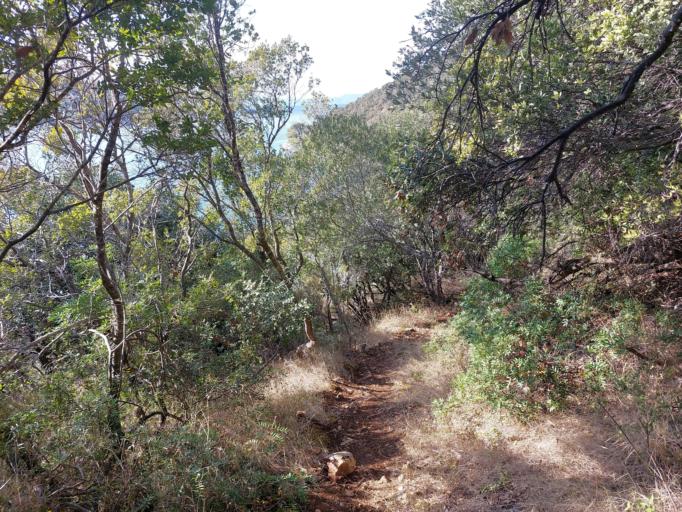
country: HR
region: Dubrovacko-Neretvanska
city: Smokvica
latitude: 42.7659
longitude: 16.8026
